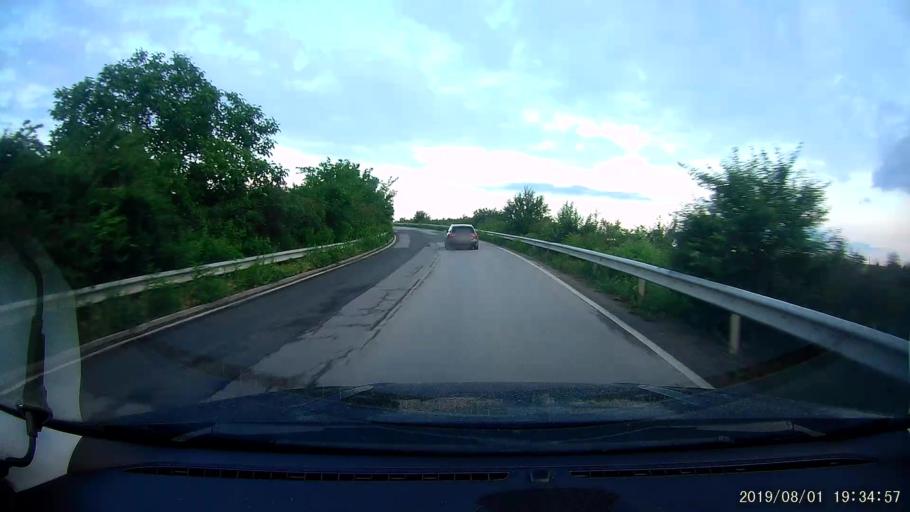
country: BG
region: Burgas
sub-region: Obshtina Sungurlare
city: Sungurlare
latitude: 42.7665
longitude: 26.8793
